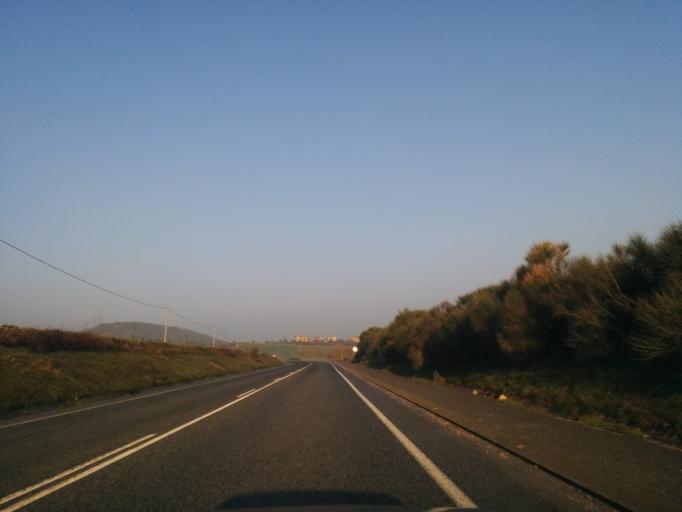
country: ES
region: Navarre
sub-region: Provincia de Navarra
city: Elorz
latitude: 42.7644
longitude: -1.5706
